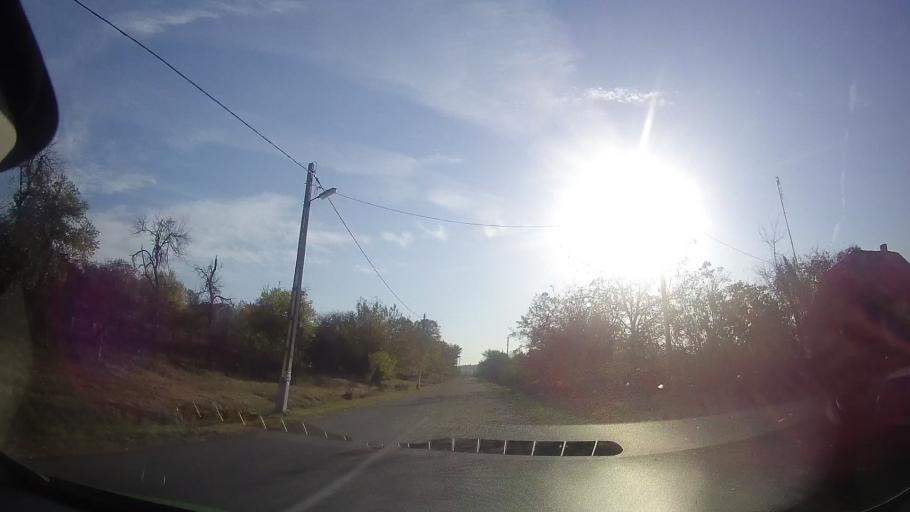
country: RO
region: Timis
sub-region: Comuna Bogda
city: Bogda
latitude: 45.9743
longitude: 21.5941
